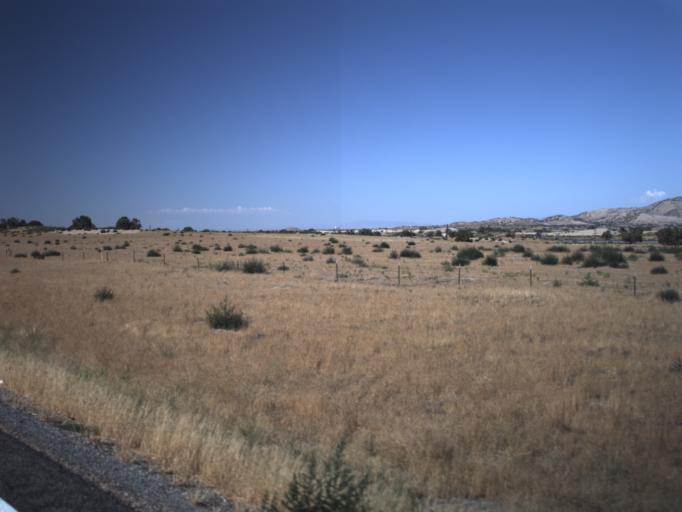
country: US
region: Utah
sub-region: Millard County
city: Delta
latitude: 39.6373
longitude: -112.3061
